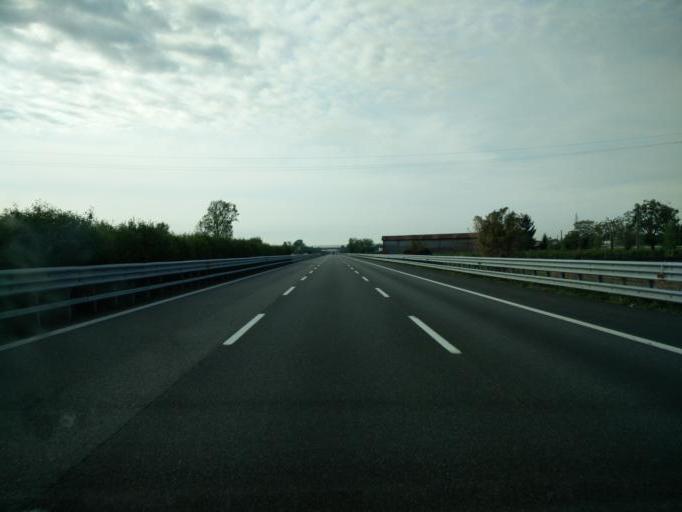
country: IT
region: Lombardy
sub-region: Provincia di Brescia
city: Bagnolo Mella
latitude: 45.4271
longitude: 10.2009
